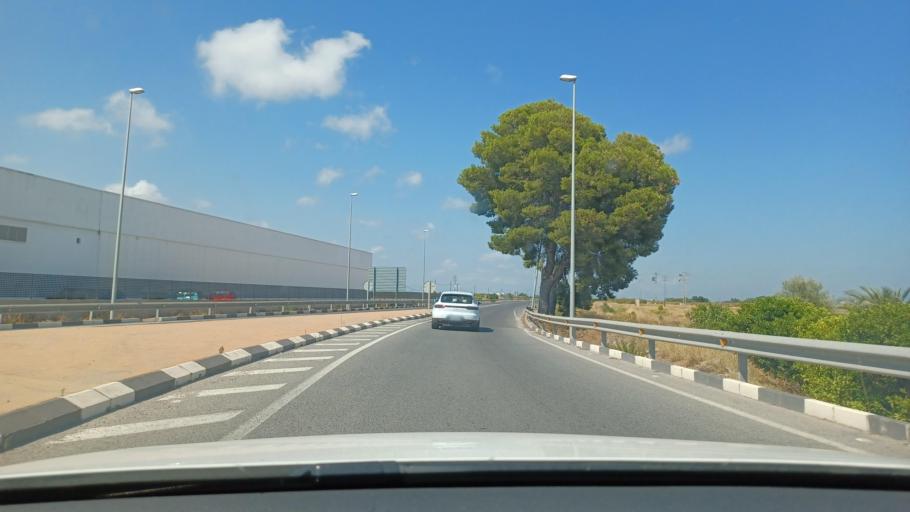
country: ES
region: Valencia
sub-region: Provincia de Castello
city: Chilches
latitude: 39.8027
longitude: -0.1751
